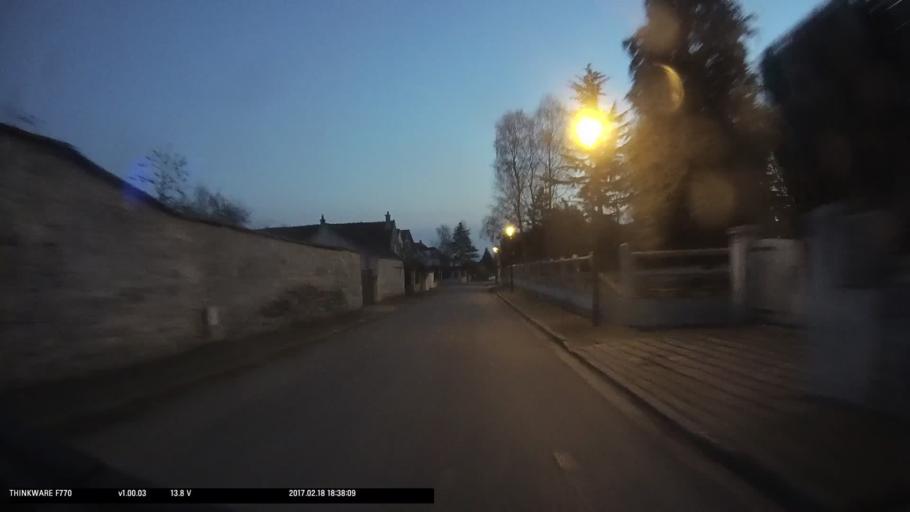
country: FR
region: Ile-de-France
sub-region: Departement du Val-d'Oise
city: Ableiges
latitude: 49.1123
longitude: 2.0152
